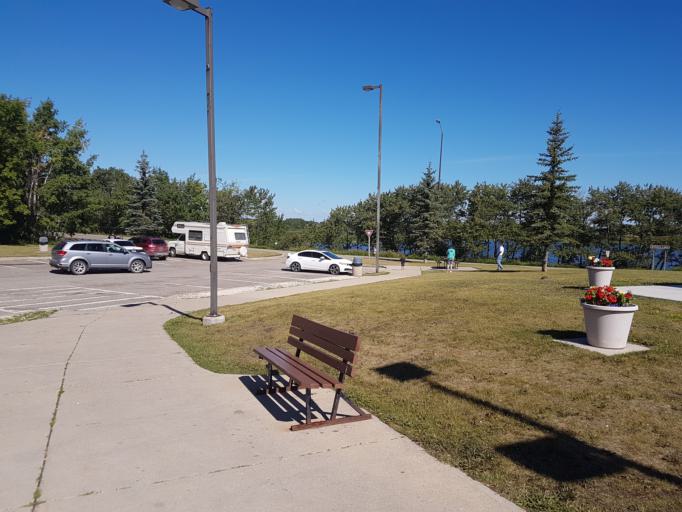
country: CA
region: Manitoba
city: Minnedosa
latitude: 50.2709
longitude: -99.9063
